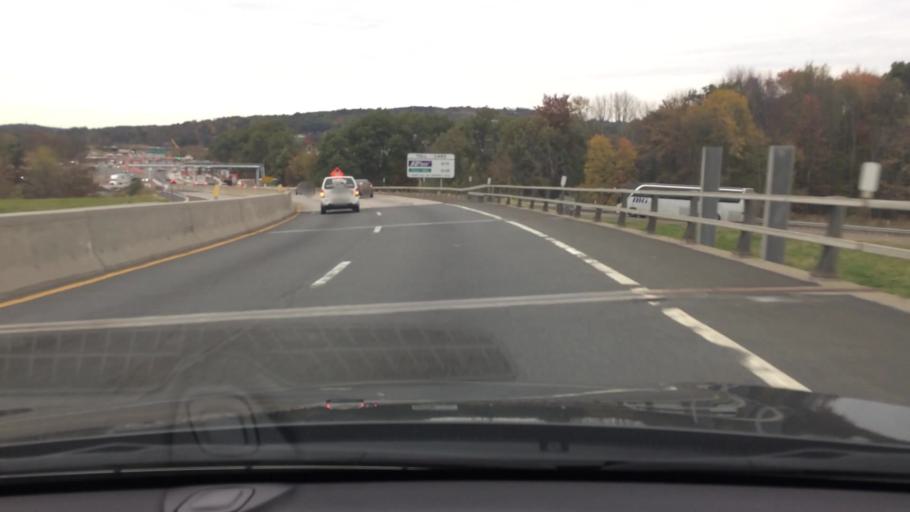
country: US
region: New York
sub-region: Orange County
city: Central Valley
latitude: 41.3110
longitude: -74.1221
